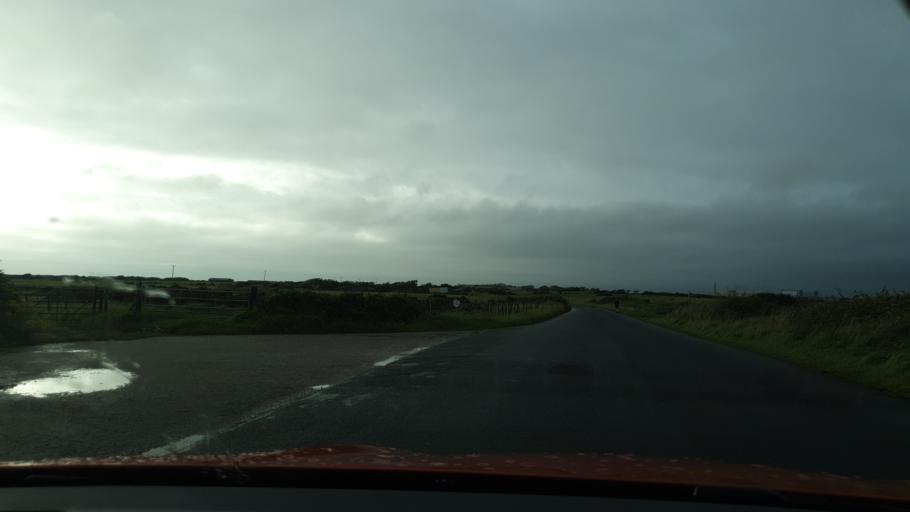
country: GB
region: England
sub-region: Cumbria
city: Barrow in Furness
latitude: 54.0773
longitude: -3.2297
